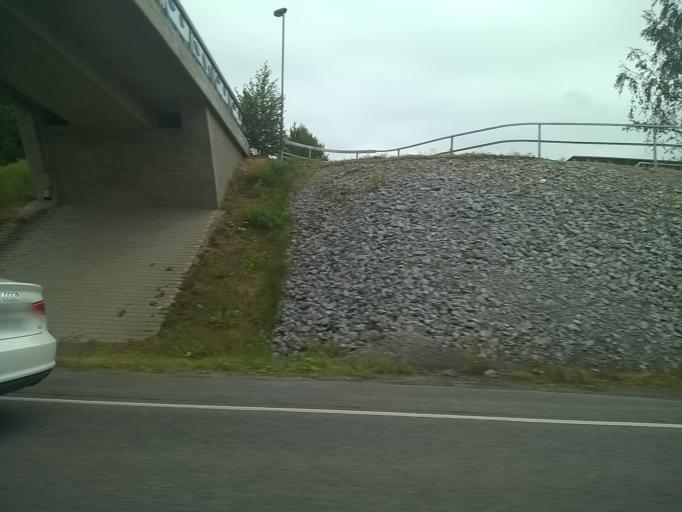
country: FI
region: Pirkanmaa
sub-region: Tampere
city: Tampere
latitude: 61.4775
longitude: 23.8336
